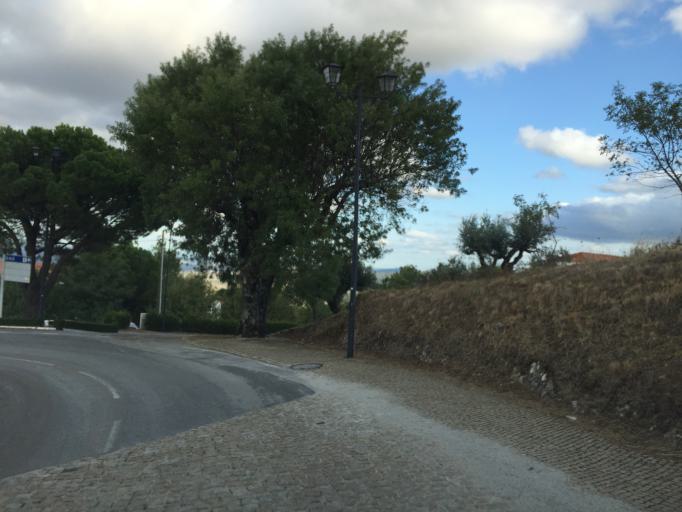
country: PT
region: Portalegre
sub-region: Marvao
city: Marvao
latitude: 39.3935
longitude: -7.3740
